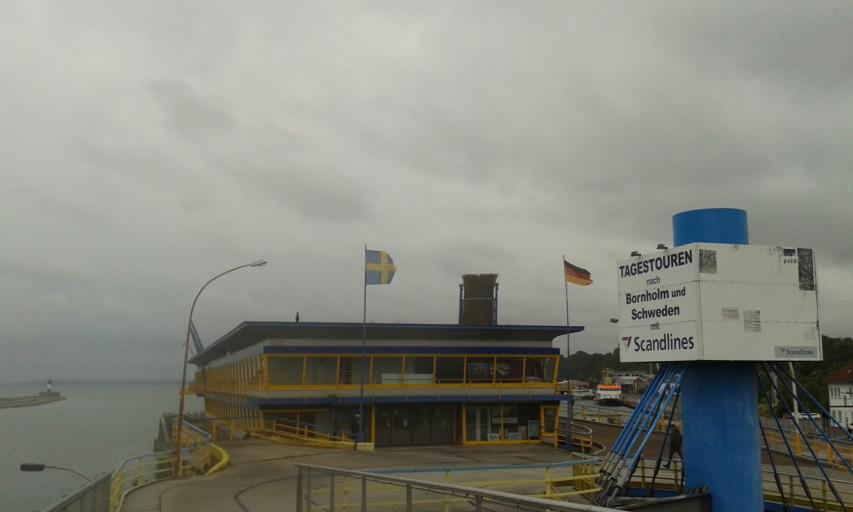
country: DE
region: Mecklenburg-Vorpommern
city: Sassnitz
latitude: 54.5122
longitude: 13.6410
